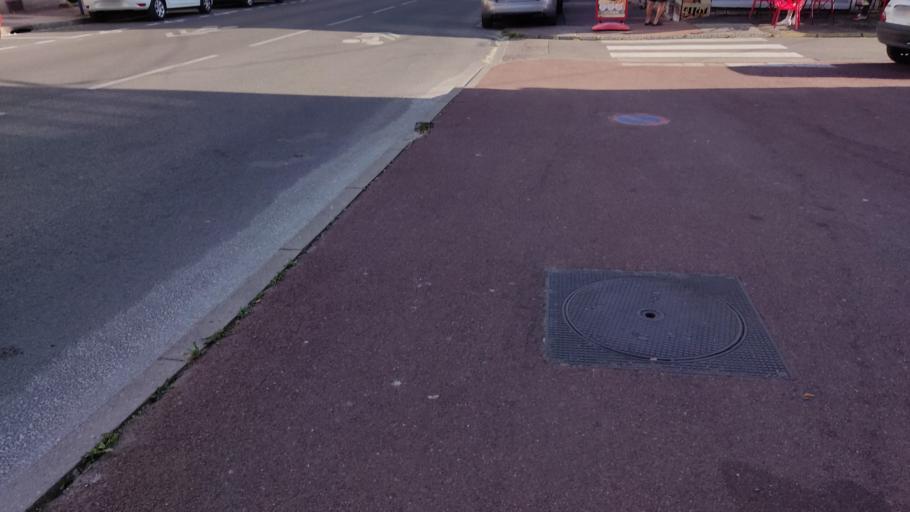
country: FR
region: Nord-Pas-de-Calais
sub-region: Departement du Pas-de-Calais
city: Le Portel
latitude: 50.7062
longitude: 1.5737
